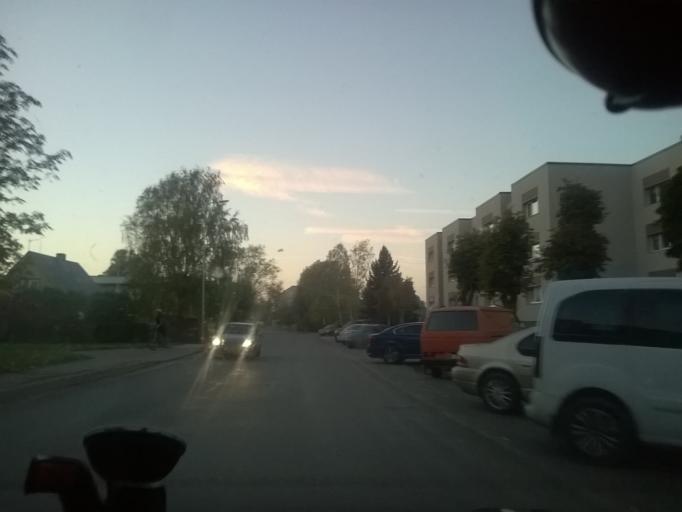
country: EE
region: Laeaene
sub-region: Haapsalu linn
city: Haapsalu
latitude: 58.9408
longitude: 23.5512
